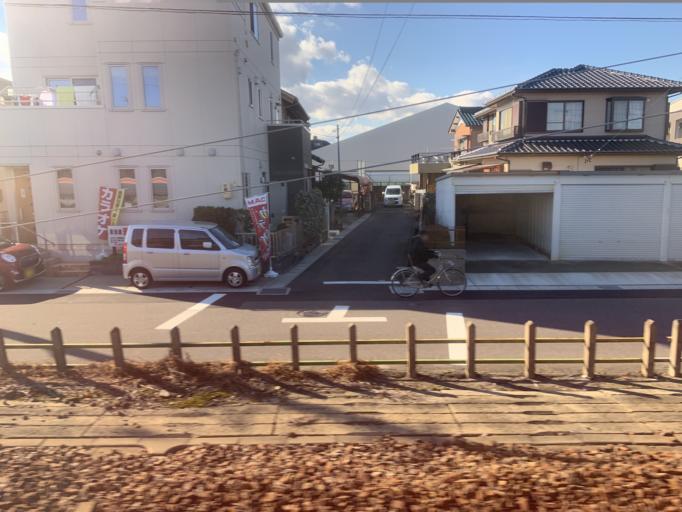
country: JP
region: Aichi
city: Kuroda
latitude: 35.3407
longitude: 136.7816
